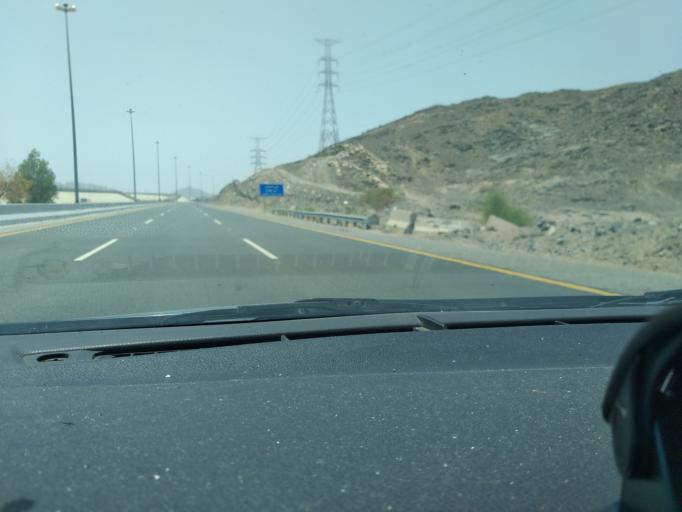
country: SA
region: Makkah
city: Mecca
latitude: 21.3271
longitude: 39.9794
